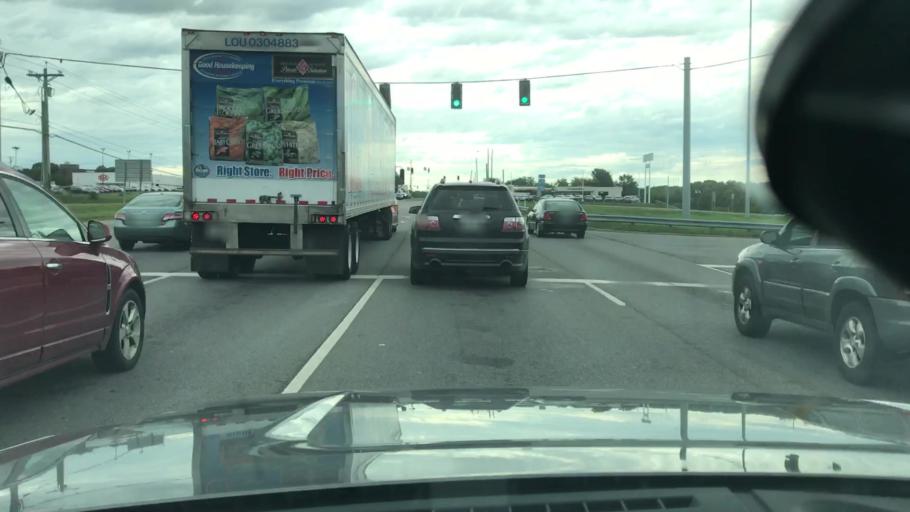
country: US
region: Tennessee
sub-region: Williamson County
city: Franklin
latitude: 35.9145
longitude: -86.8256
